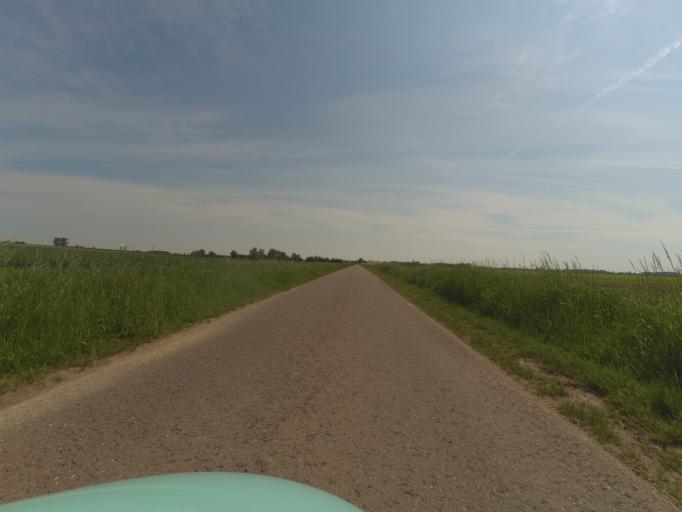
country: DE
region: Lower Saxony
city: Hohenhameln
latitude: 52.2686
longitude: 10.0240
